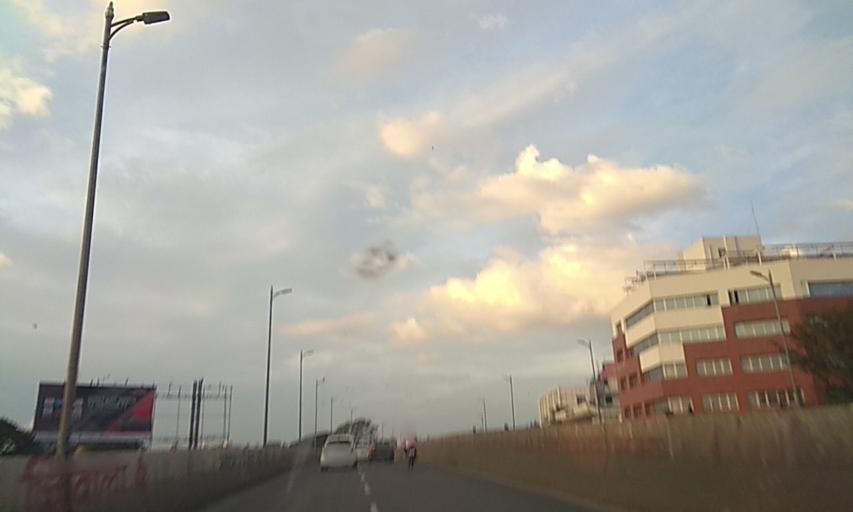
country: IN
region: Maharashtra
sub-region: Pune Division
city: Pune
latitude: 18.4959
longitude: 73.8577
